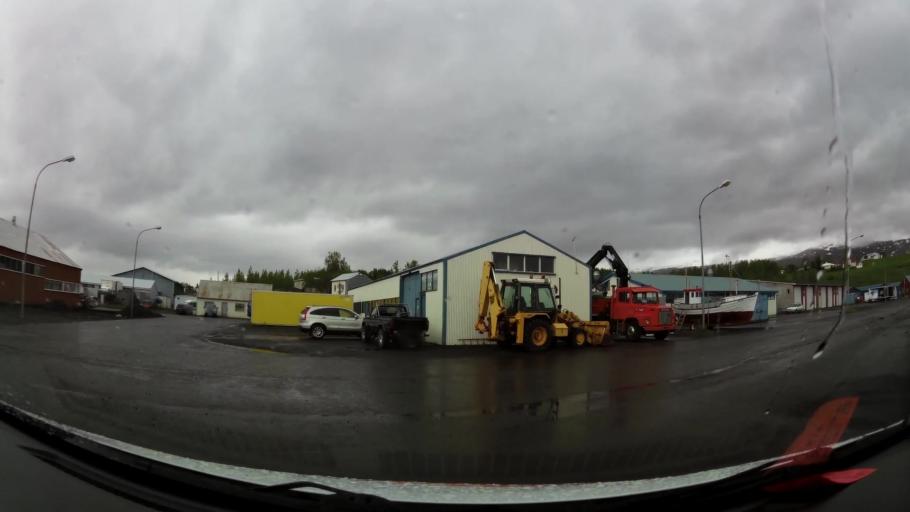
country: IS
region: Northeast
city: Akureyri
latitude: 65.6951
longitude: -18.1031
